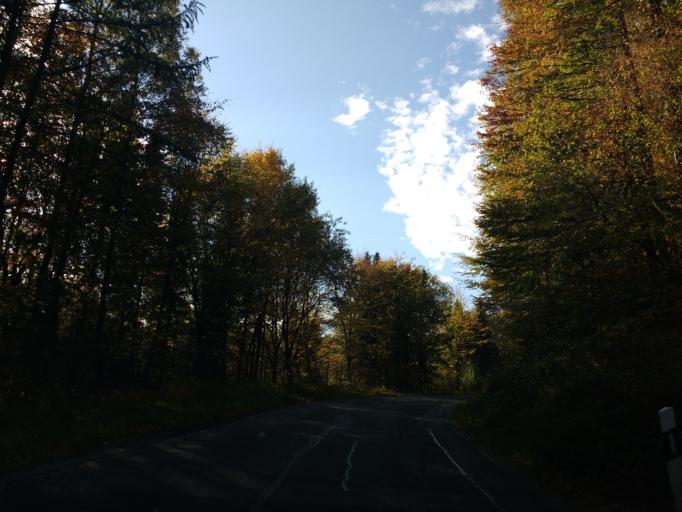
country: DE
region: North Rhine-Westphalia
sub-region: Regierungsbezirk Arnsberg
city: Bestwig
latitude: 51.3115
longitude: 8.4385
